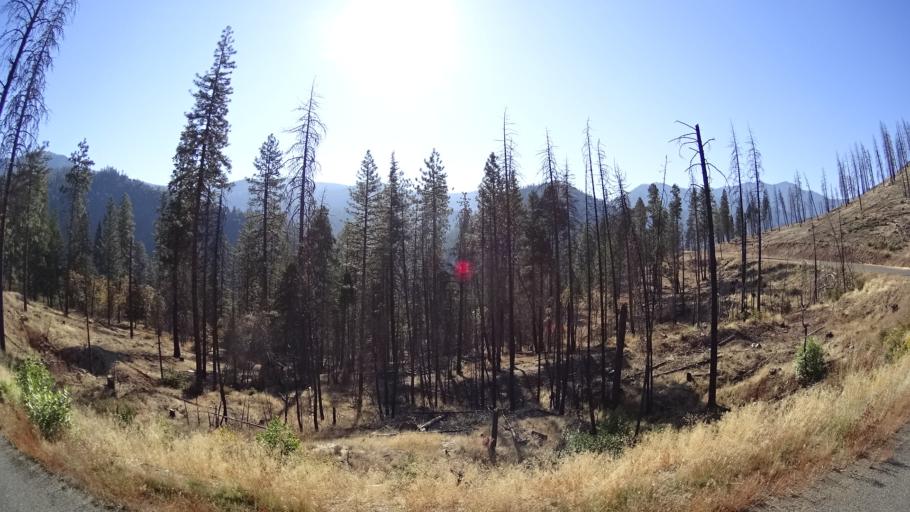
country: US
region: California
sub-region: Siskiyou County
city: Happy Camp
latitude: 41.7307
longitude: -123.0123
